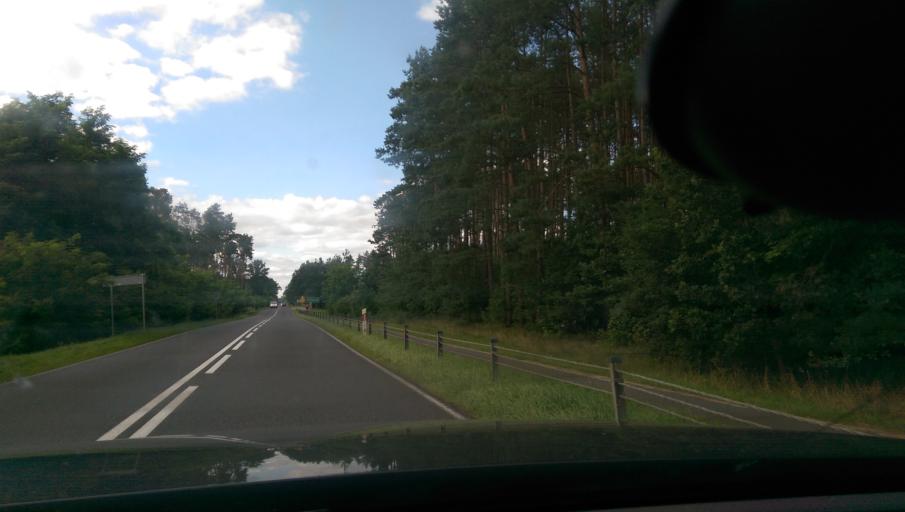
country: PL
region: Lubusz
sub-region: Powiat slubicki
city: Osno Lubuskie
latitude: 52.4889
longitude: 14.9120
